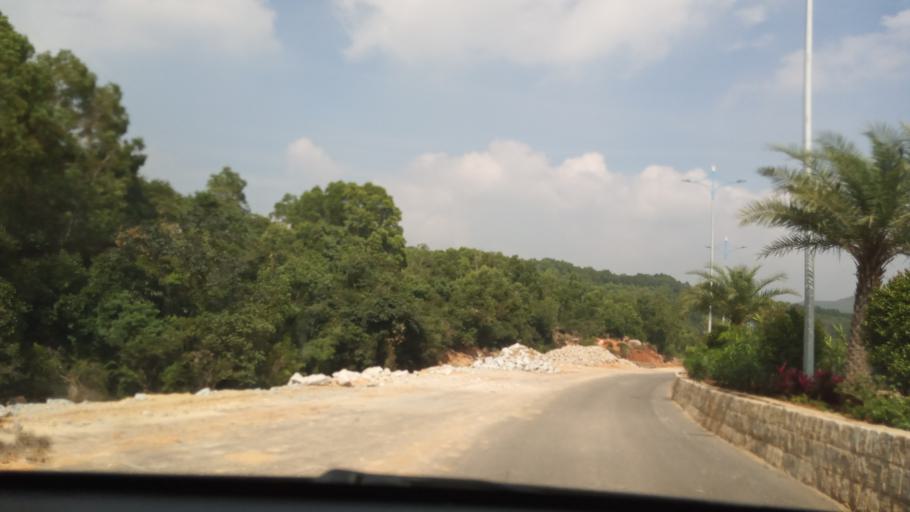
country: IN
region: Andhra Pradesh
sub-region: Chittoor
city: Tirumala
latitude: 13.6890
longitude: 79.3432
